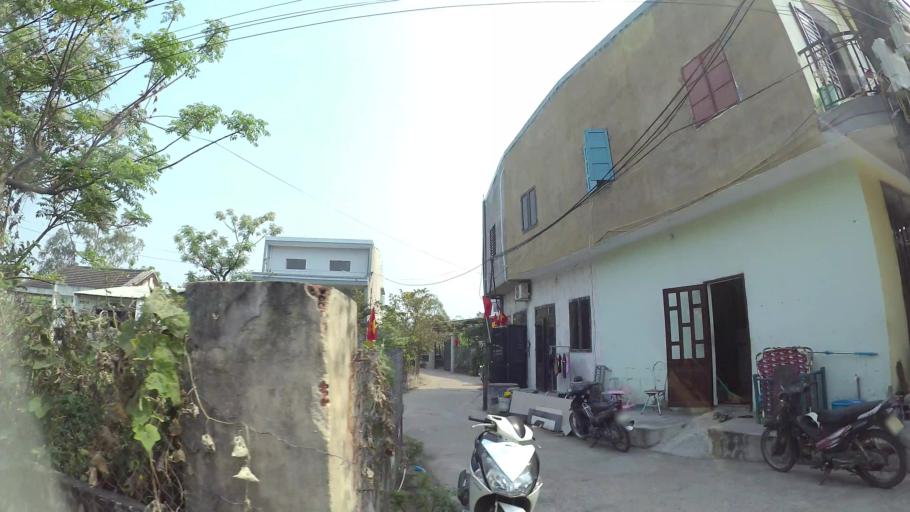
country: VN
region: Da Nang
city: Ngu Hanh Son
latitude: 15.9915
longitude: 108.2414
